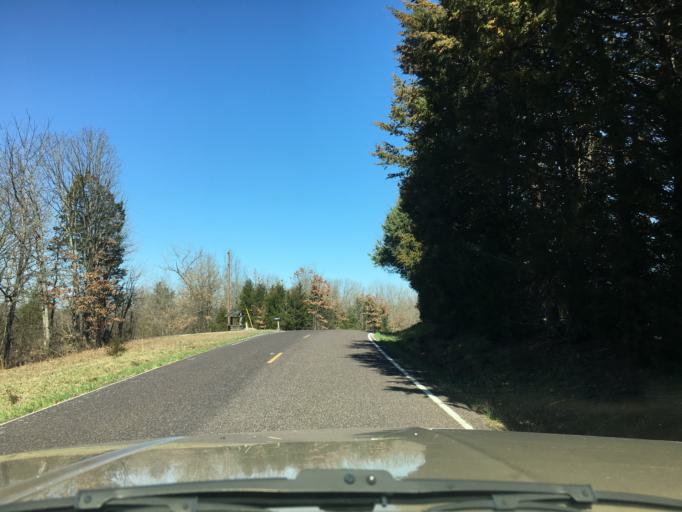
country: US
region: Missouri
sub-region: Franklin County
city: Gerald
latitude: 38.5205
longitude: -91.3285
